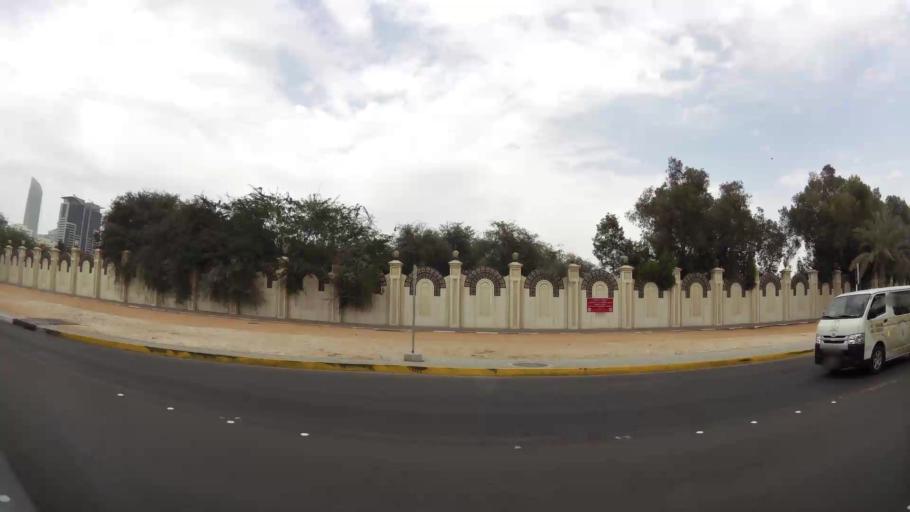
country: AE
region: Abu Dhabi
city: Abu Dhabi
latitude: 24.4704
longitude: 54.3531
